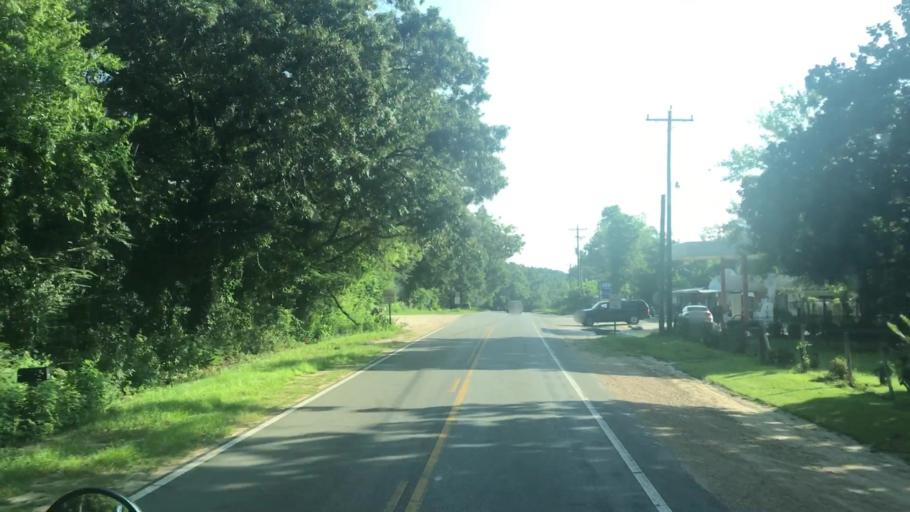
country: US
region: Florida
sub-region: Gadsden County
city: Quincy
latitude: 30.6502
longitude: -84.5699
